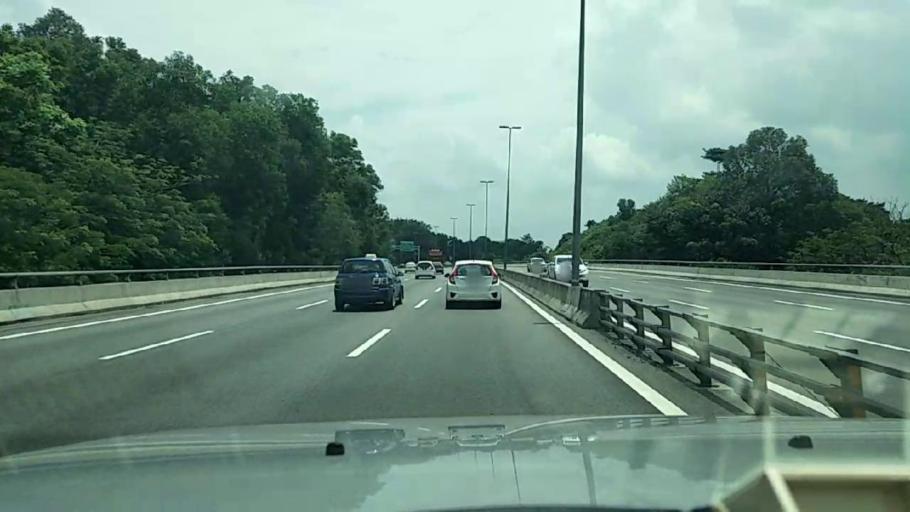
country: MY
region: Selangor
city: Kampong Baharu Balakong
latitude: 3.0564
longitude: 101.6885
